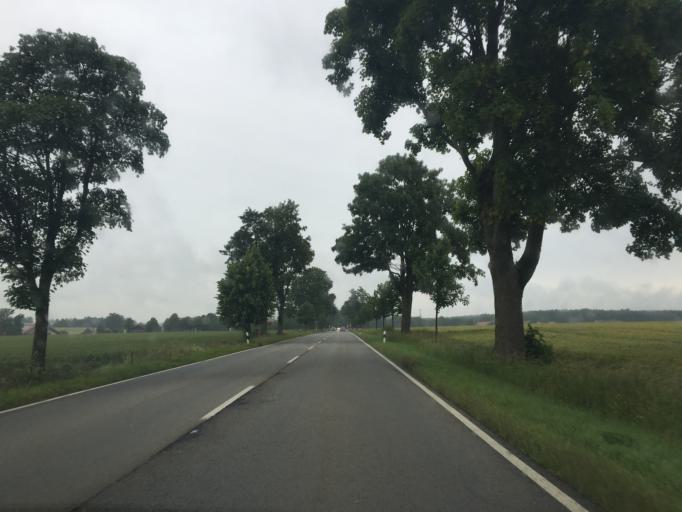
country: DE
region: Bavaria
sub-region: Upper Bavaria
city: Holzkirchen
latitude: 47.8680
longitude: 11.7184
